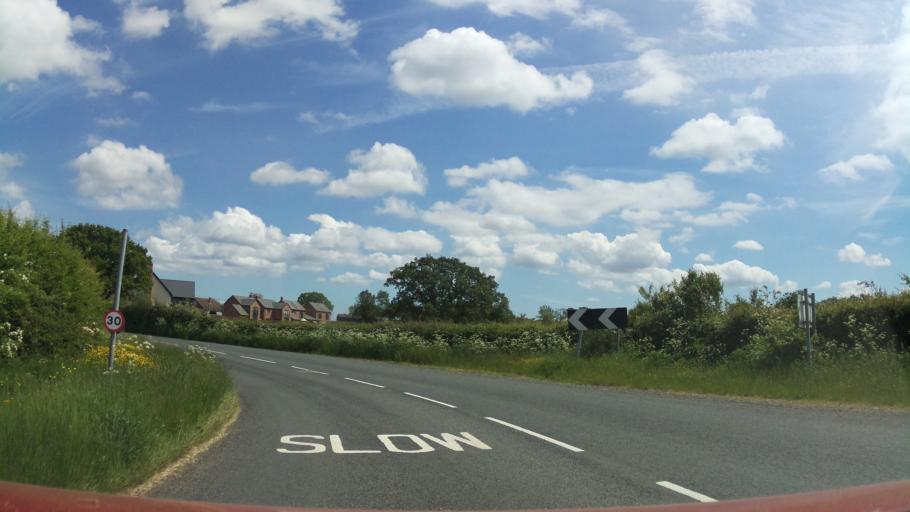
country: GB
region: England
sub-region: Herefordshire
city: Llanrothal
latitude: 51.8875
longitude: -2.7587
